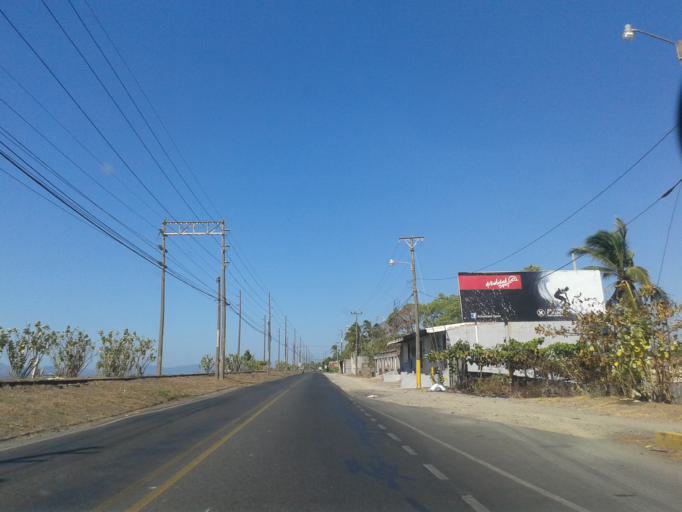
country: CR
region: Puntarenas
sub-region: Canton Central de Puntarenas
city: Chacarita
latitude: 9.9806
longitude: -84.7932
